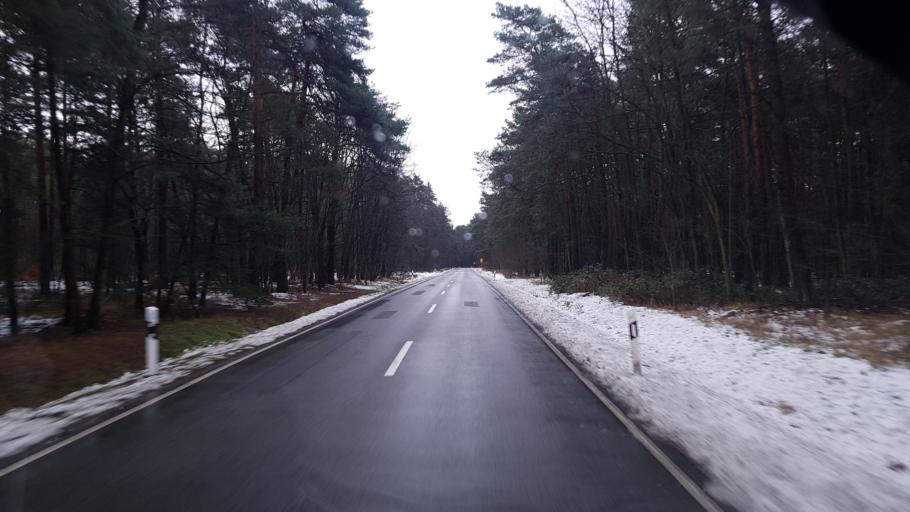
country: DE
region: Brandenburg
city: Schenkendobern
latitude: 51.9052
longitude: 14.6316
